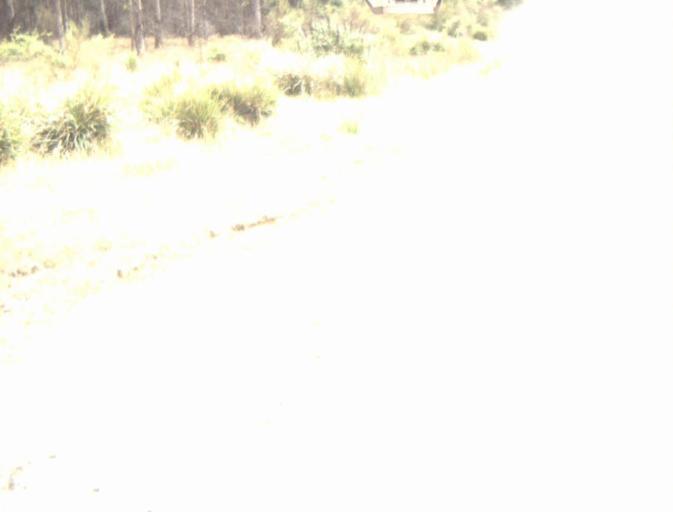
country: AU
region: Tasmania
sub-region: Northern Midlands
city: Evandale
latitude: -41.4528
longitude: 147.4765
